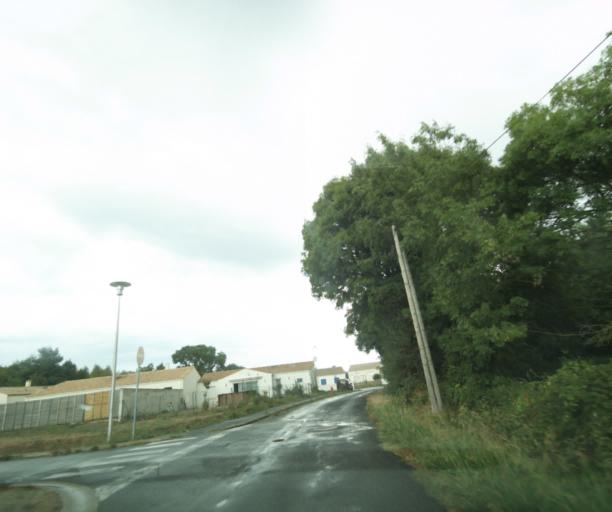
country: FR
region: Poitou-Charentes
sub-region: Departement de la Charente-Maritime
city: Tonnay-Charente
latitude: 45.9432
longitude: -0.8778
